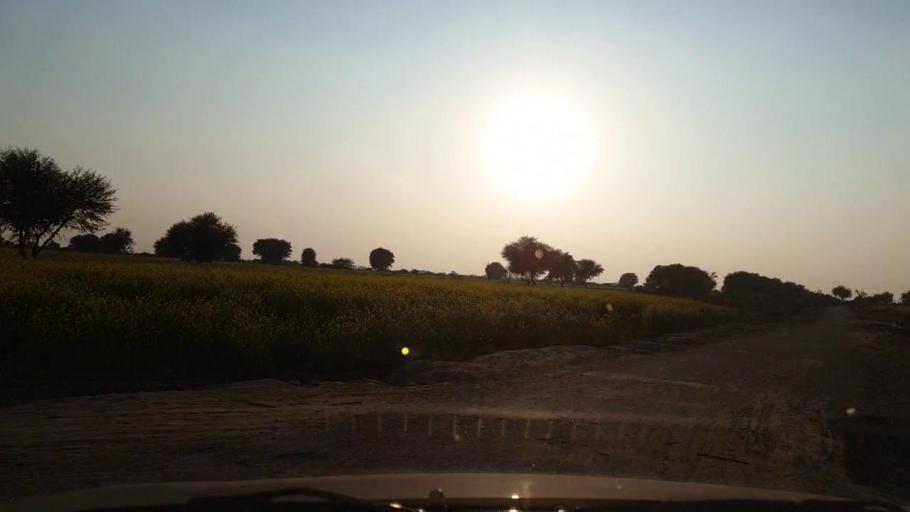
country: PK
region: Sindh
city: Jhol
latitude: 25.9115
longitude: 68.9337
